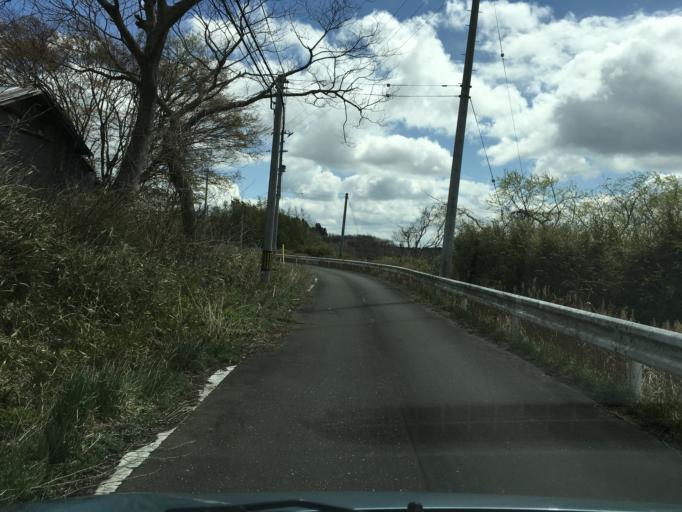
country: JP
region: Miyagi
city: Wakuya
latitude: 38.6914
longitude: 141.1024
